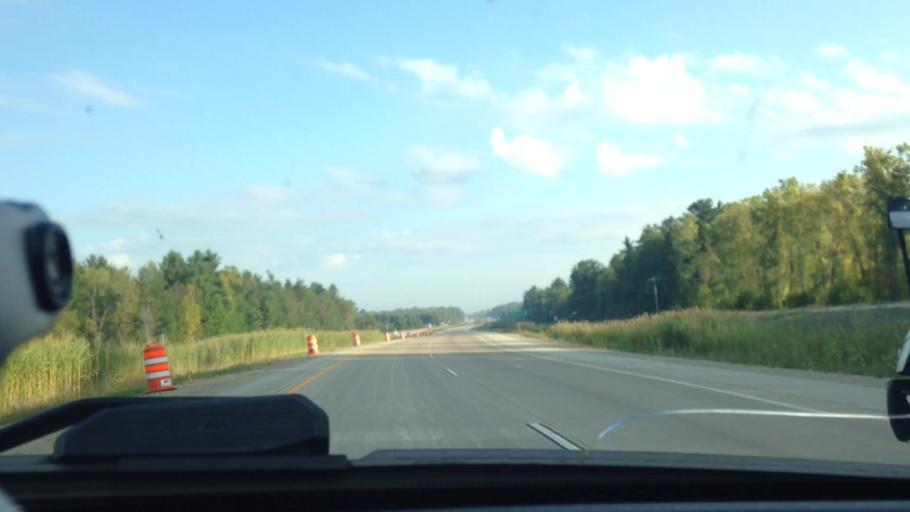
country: US
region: Wisconsin
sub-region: Oconto County
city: Oconto Falls
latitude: 44.7961
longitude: -88.0496
